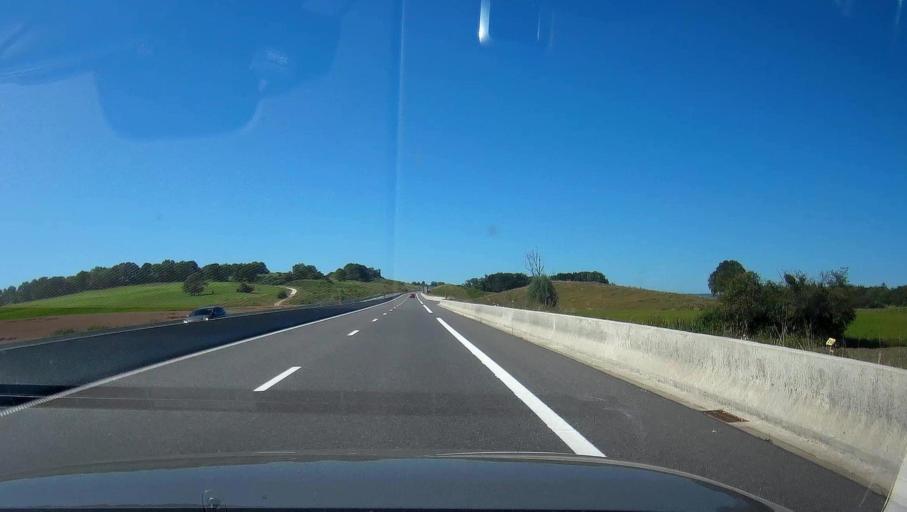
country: FR
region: Champagne-Ardenne
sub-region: Departement des Ardennes
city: Tournes
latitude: 49.7682
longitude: 4.6360
